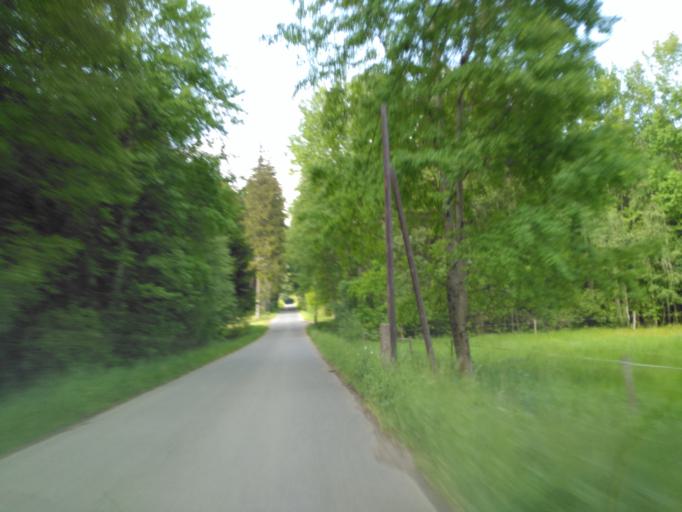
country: CZ
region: Plzensky
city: Zbiroh
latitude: 49.8969
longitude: 13.8094
